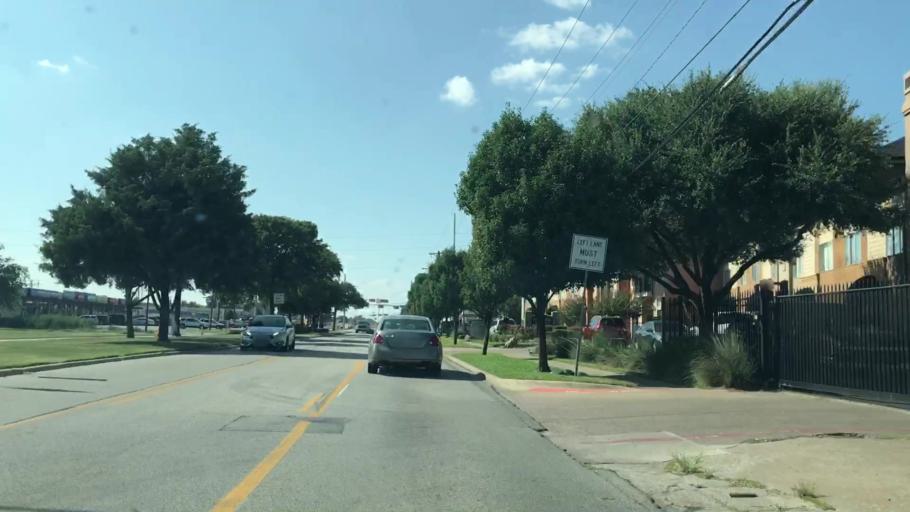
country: US
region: Texas
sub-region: Dallas County
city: Mesquite
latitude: 32.8211
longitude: -96.6431
